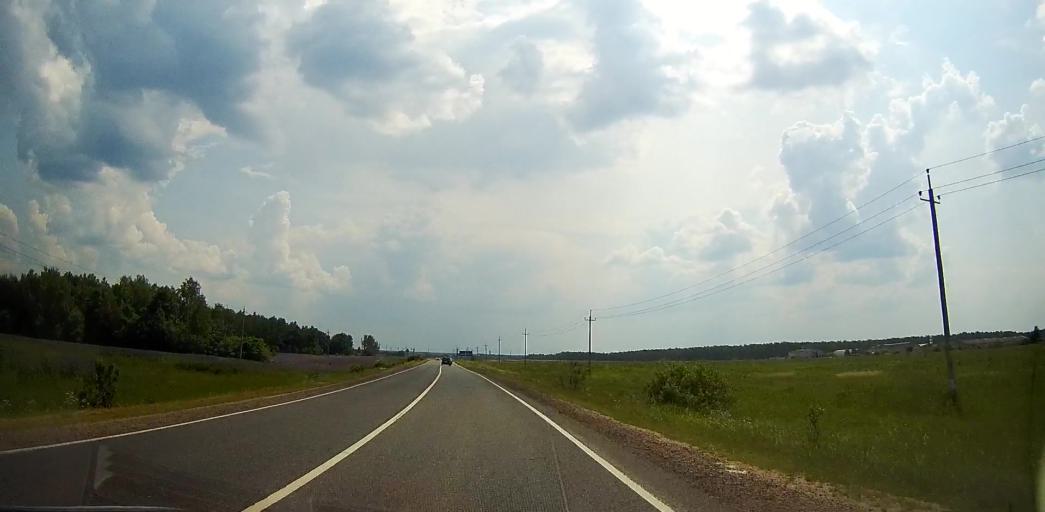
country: RU
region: Moskovskaya
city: Stupino
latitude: 54.9610
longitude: 38.1229
